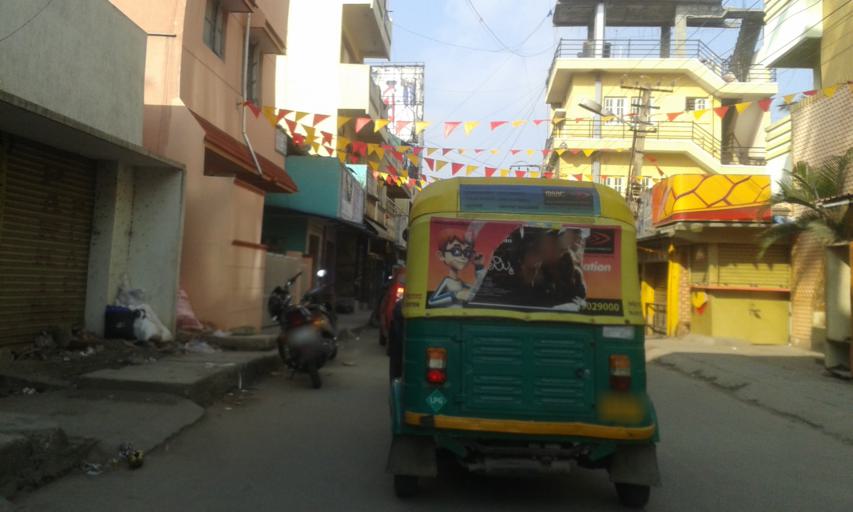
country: IN
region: Karnataka
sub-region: Bangalore Urban
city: Bangalore
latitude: 12.9441
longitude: 77.6180
